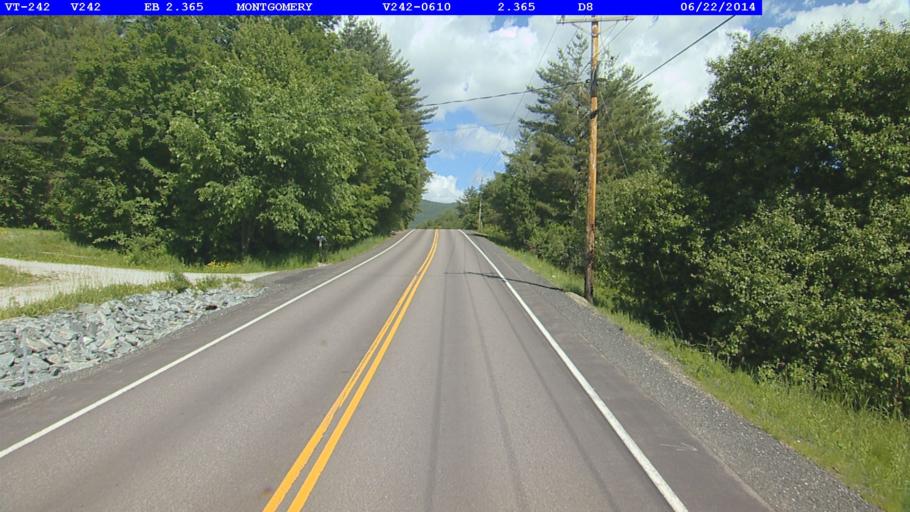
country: US
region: Vermont
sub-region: Franklin County
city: Richford
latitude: 44.8815
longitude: -72.5653
